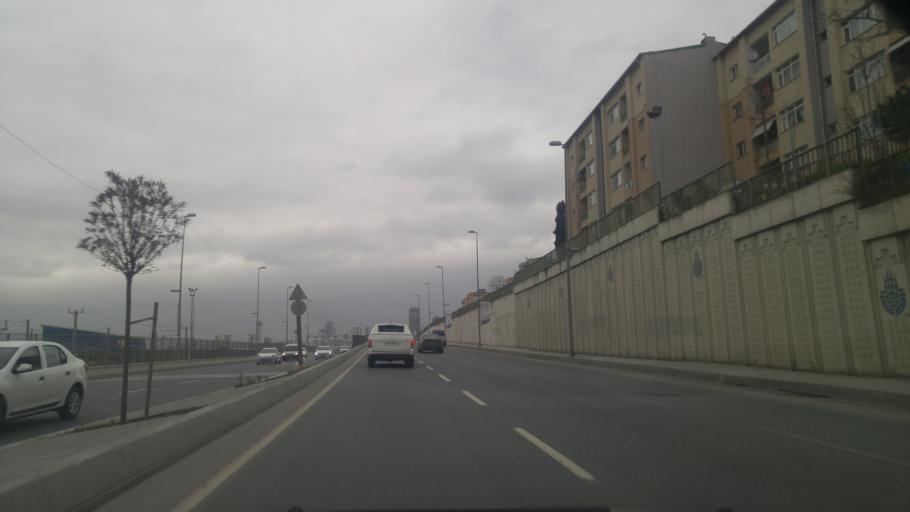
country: TR
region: Istanbul
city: Mahmutbey
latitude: 41.0226
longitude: 28.7676
